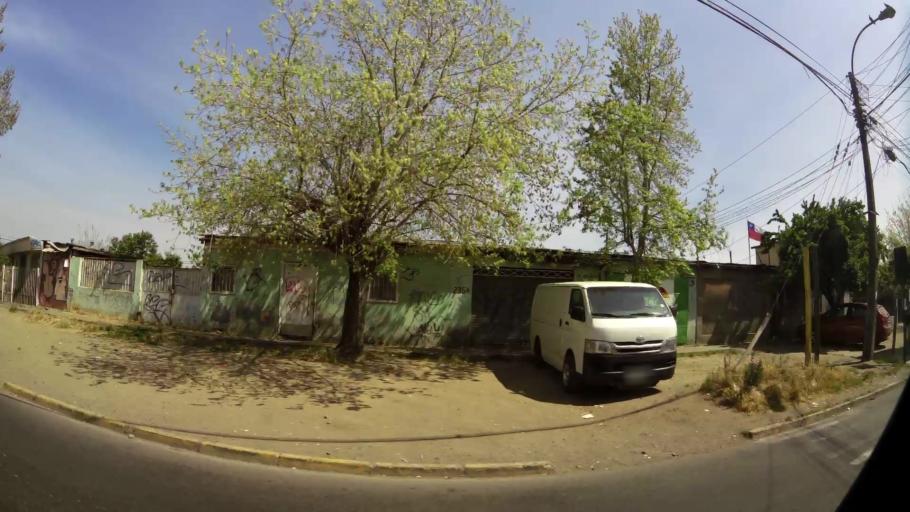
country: CL
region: Santiago Metropolitan
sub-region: Provincia de Santiago
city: Lo Prado
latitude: -33.4186
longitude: -70.7034
